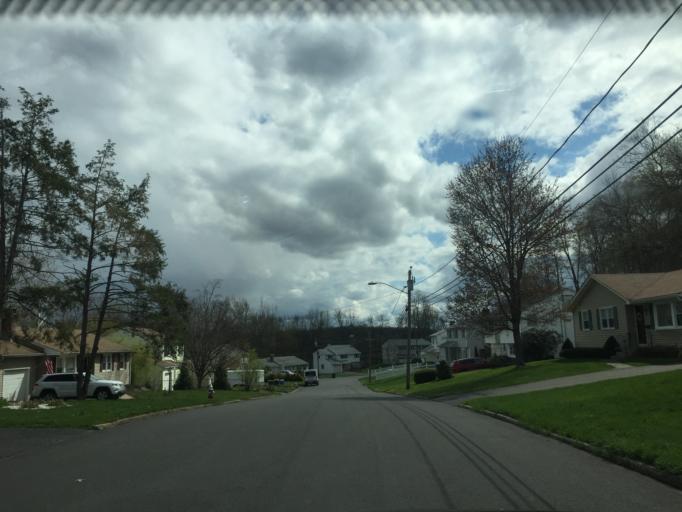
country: US
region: Connecticut
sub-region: Hartford County
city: New Britain
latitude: 41.7104
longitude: -72.7795
